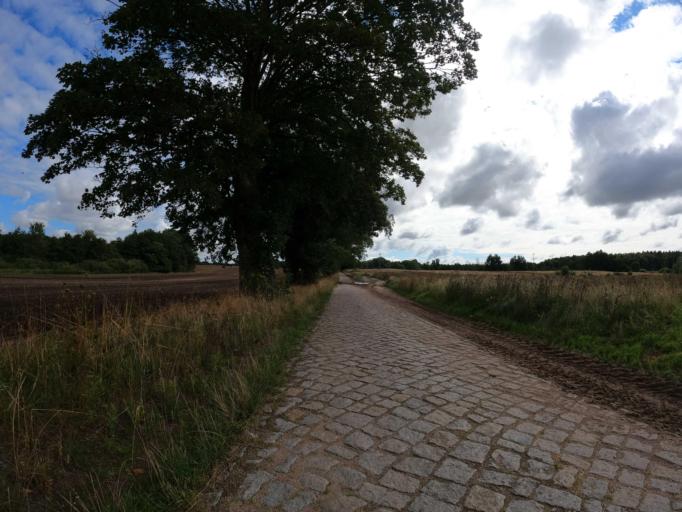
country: DE
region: Mecklenburg-Vorpommern
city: Samtens
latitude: 54.3610
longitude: 13.3129
